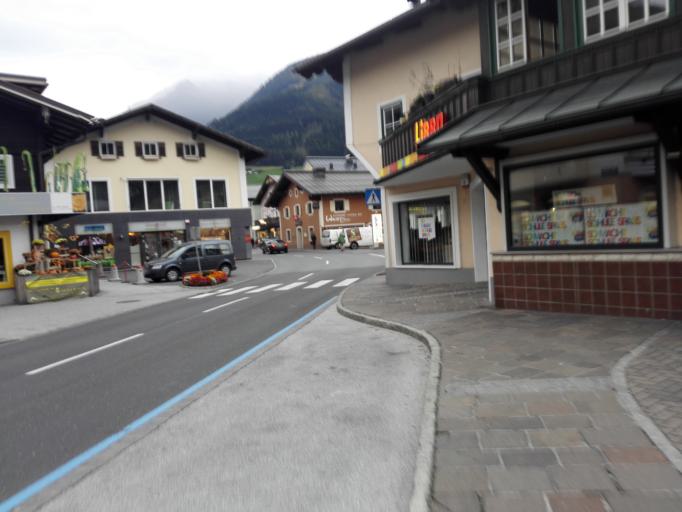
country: AT
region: Salzburg
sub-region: Politischer Bezirk Zell am See
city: Mittersill
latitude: 47.2824
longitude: 12.4825
